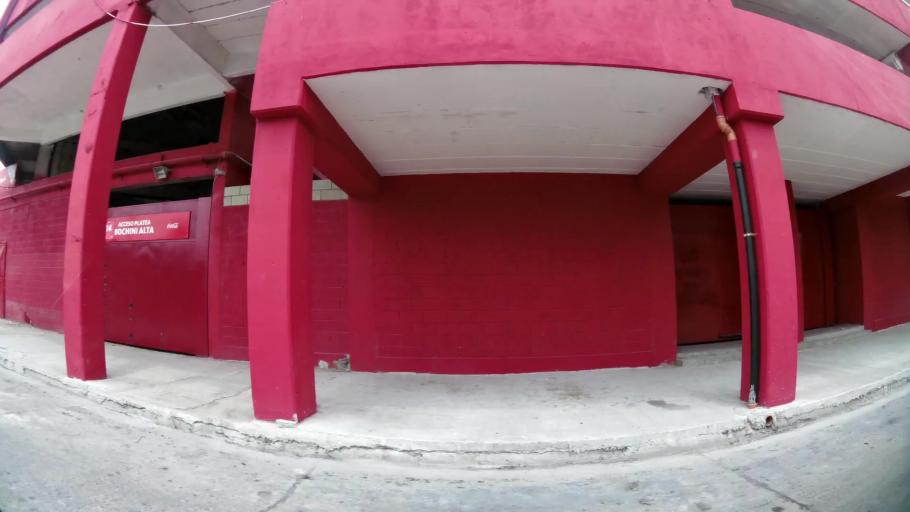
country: AR
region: Buenos Aires
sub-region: Partido de Avellaneda
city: Avellaneda
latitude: -34.6701
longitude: -58.3699
